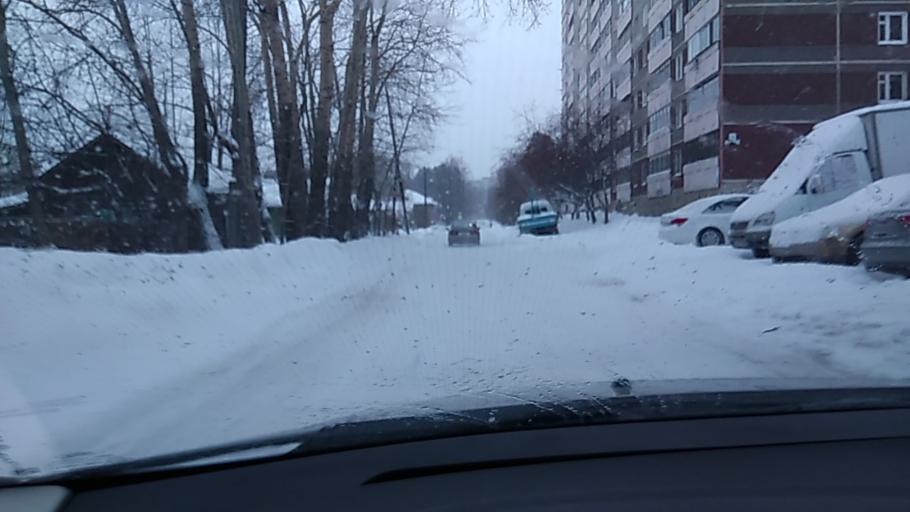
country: RU
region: Sverdlovsk
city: Sovkhoznyy
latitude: 56.8197
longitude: 60.5461
